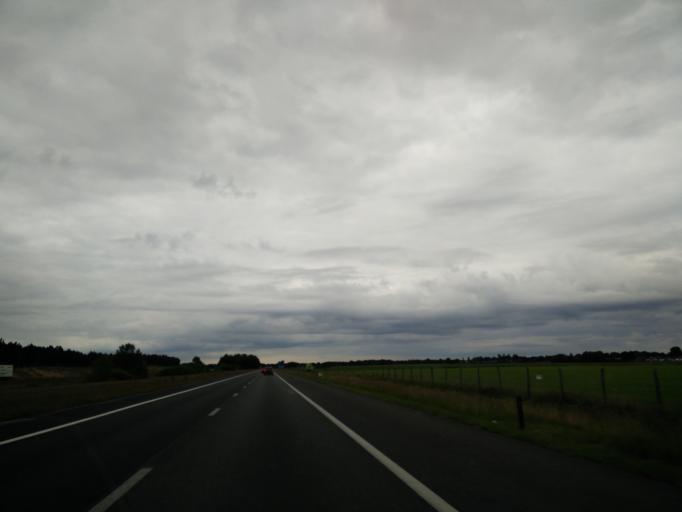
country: NL
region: Drenthe
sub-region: Gemeente Hoogeveen
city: Hoogeveen
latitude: 52.7948
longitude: 6.4524
